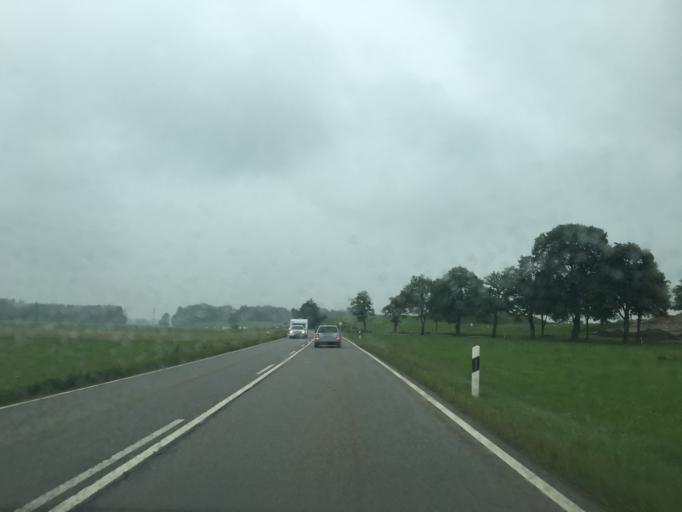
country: DE
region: Bavaria
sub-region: Upper Bavaria
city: Warngau
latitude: 47.8418
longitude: 11.7197
